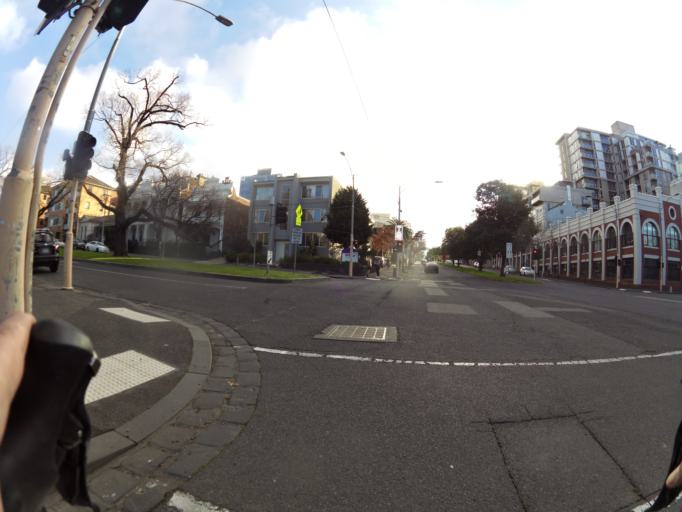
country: AU
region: Victoria
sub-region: Melbourne
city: East Melbourne
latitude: -37.8108
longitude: 144.9862
